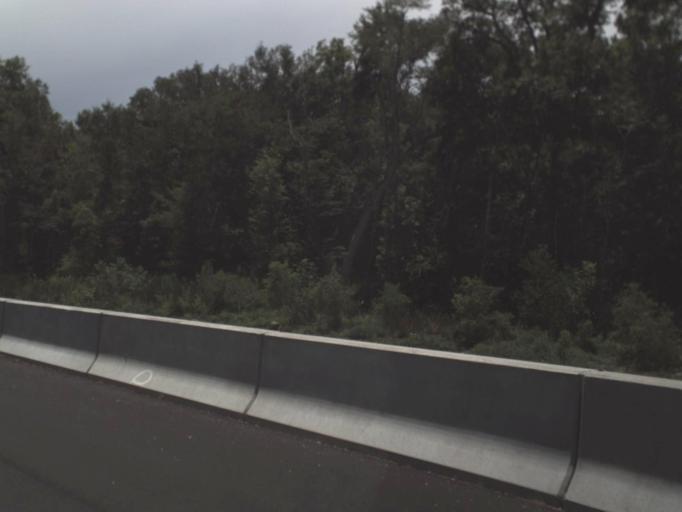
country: US
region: Florida
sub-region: Leon County
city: Woodville
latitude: 30.1446
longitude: -83.9697
